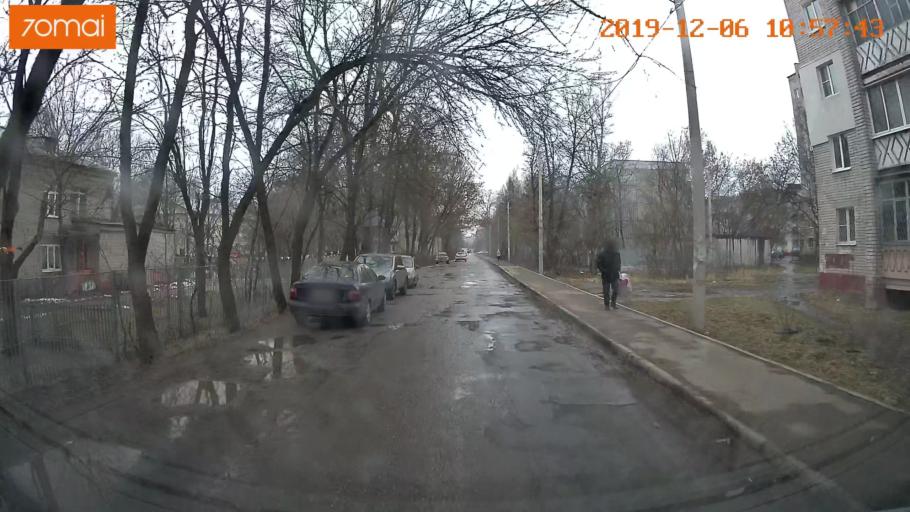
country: RU
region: Ivanovo
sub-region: Gorod Ivanovo
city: Ivanovo
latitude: 56.9676
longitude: 40.9777
